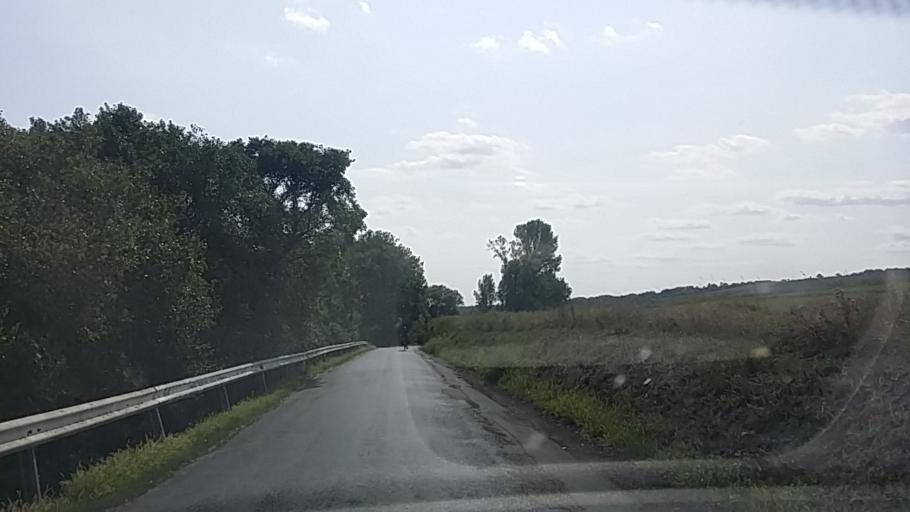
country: HU
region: Gyor-Moson-Sopron
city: Fertorakos
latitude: 47.6709
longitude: 16.6717
